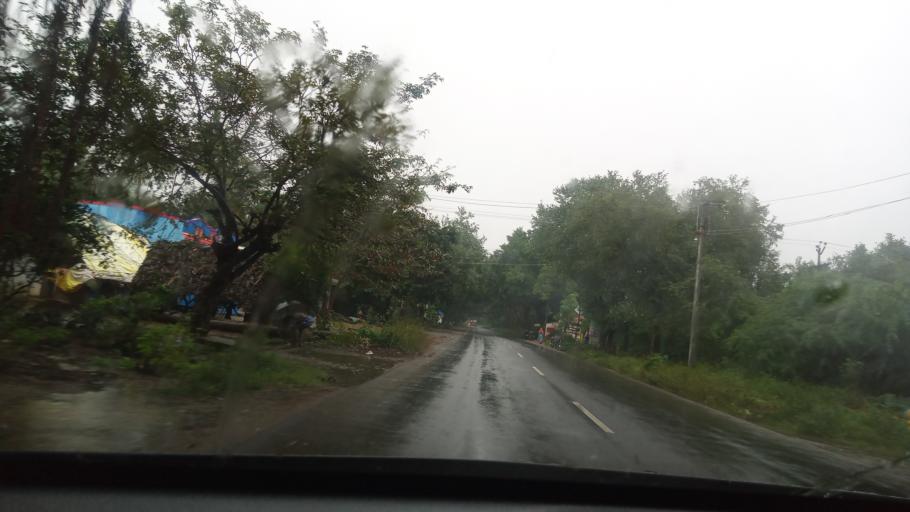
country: IN
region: Tamil Nadu
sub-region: Vellore
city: Kalavai
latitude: 12.8066
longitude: 79.4141
